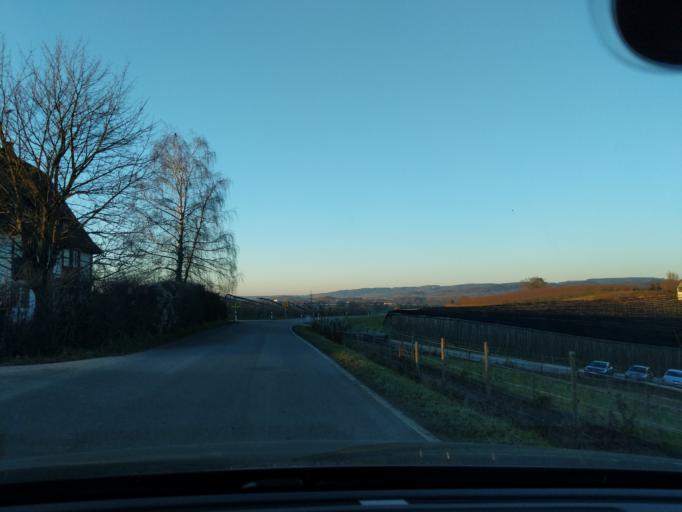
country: DE
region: Baden-Wuerttemberg
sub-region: Tuebingen Region
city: Bermatingen
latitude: 47.7036
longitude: 9.3388
